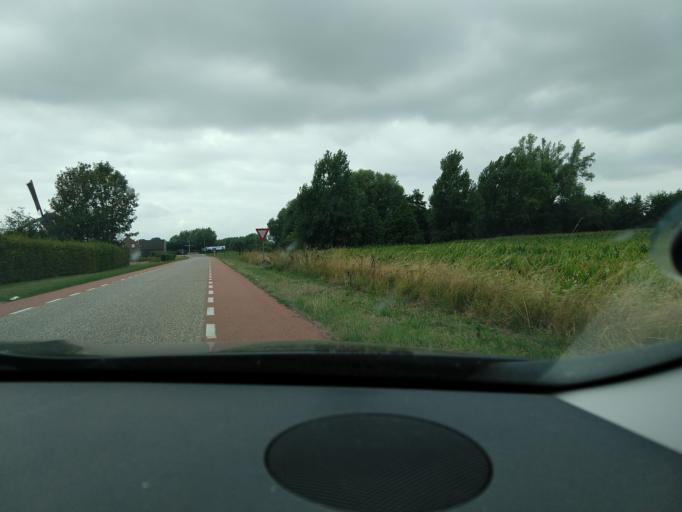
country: NL
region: Zeeland
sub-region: Gemeente Hulst
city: Hulst
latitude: 51.3384
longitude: 4.0379
